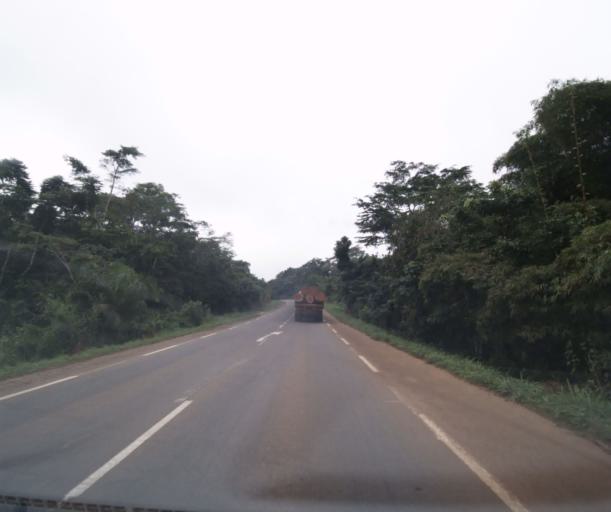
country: CM
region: Centre
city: Mbankomo
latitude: 3.7656
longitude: 11.1281
